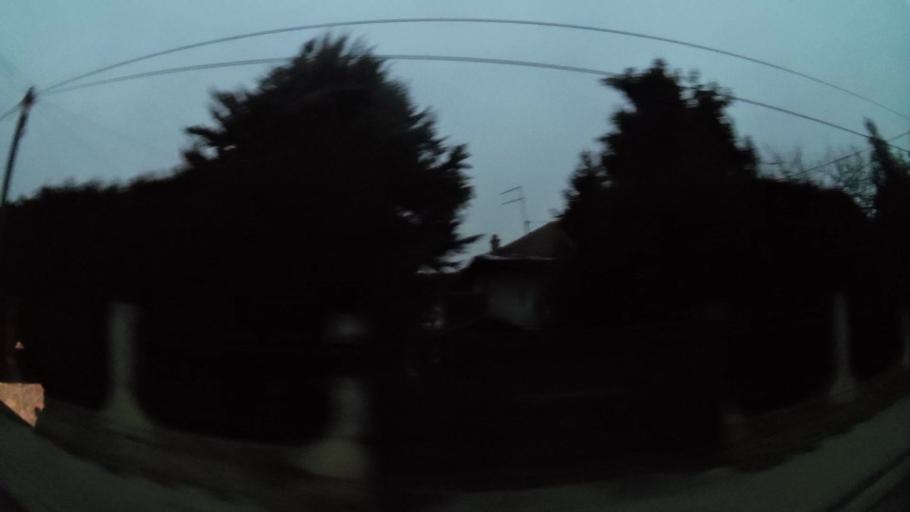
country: MK
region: Kisela Voda
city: Kisela Voda
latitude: 41.9673
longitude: 21.4887
